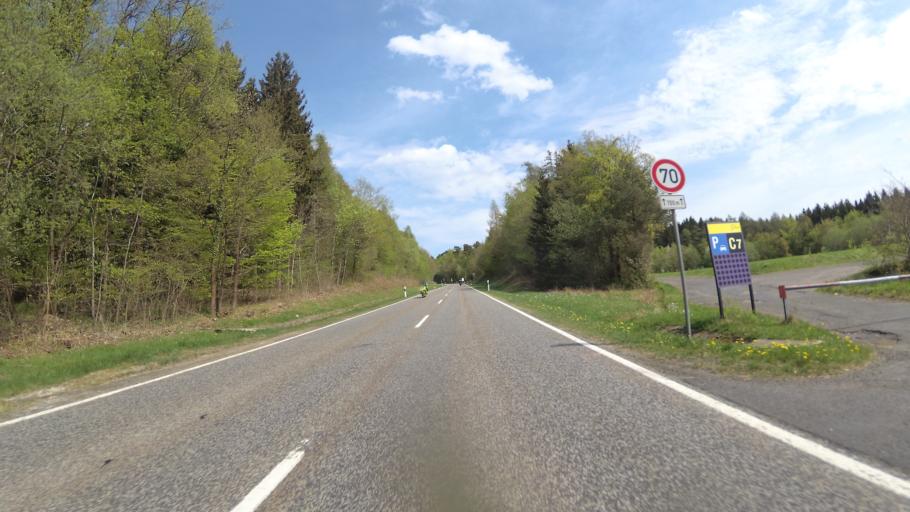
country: DE
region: Rheinland-Pfalz
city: Mullenbach
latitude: 50.3279
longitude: 6.9274
